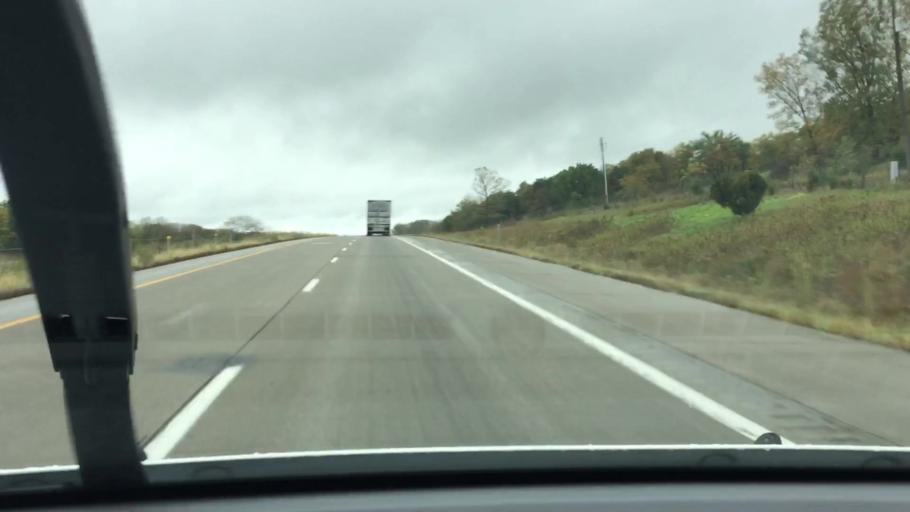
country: US
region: Iowa
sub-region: Jasper County
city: Colfax
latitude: 41.6868
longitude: -93.2751
